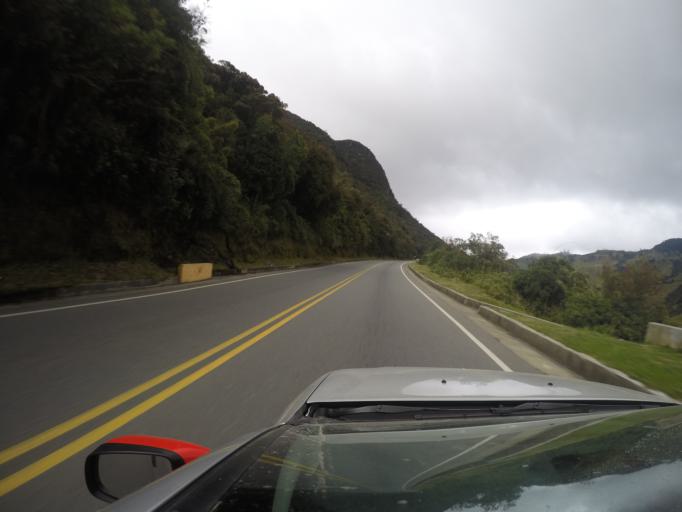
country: CO
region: Tolima
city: Herveo
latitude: 5.0244
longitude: -75.3343
